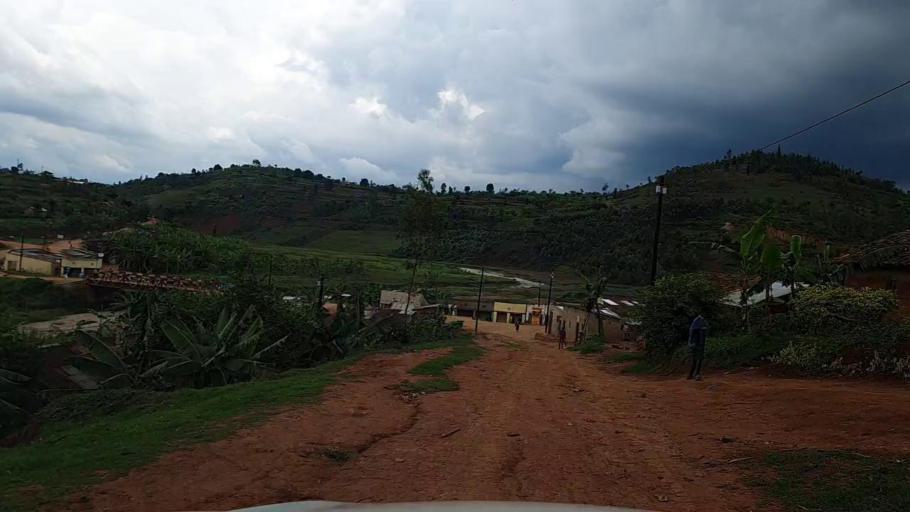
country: RW
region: Southern Province
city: Gikongoro
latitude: -2.4173
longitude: 29.6629
